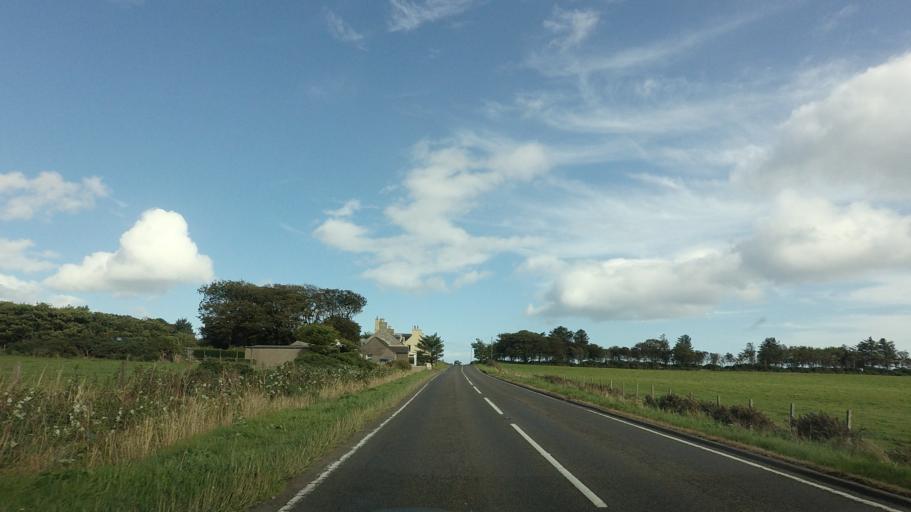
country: GB
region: Scotland
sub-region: Highland
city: Wick
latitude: 58.3007
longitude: -3.3105
